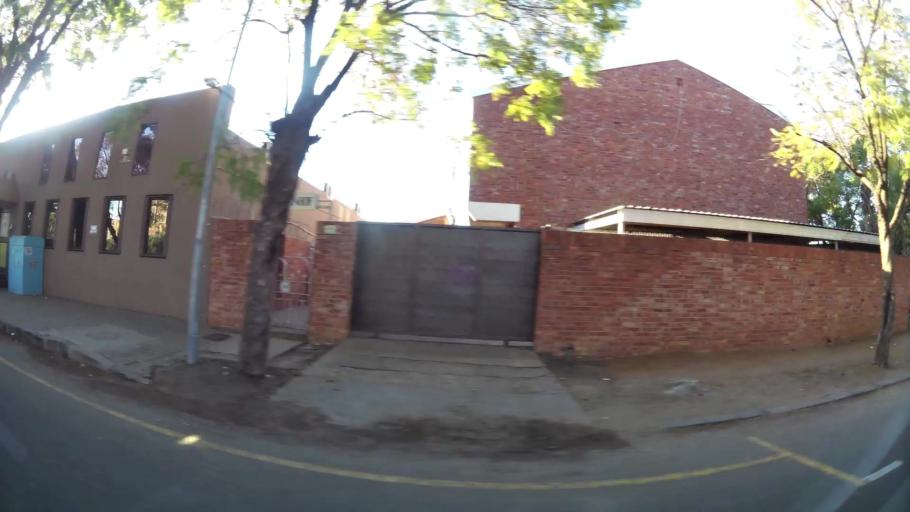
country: ZA
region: Northern Cape
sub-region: Frances Baard District Municipality
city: Kimberley
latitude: -28.7358
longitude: 24.7662
